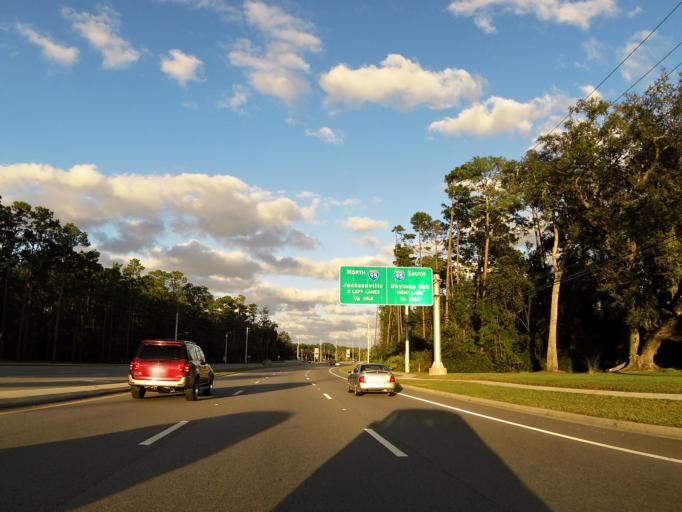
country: US
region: Florida
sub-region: Saint Johns County
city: Fruit Cove
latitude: 30.0638
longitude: -81.5034
